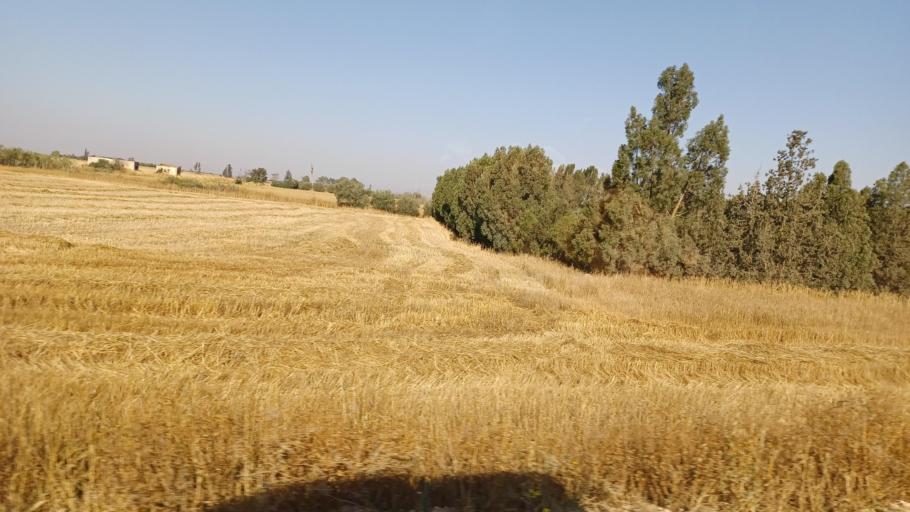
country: CY
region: Ammochostos
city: Frenaros
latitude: 35.0821
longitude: 33.9111
